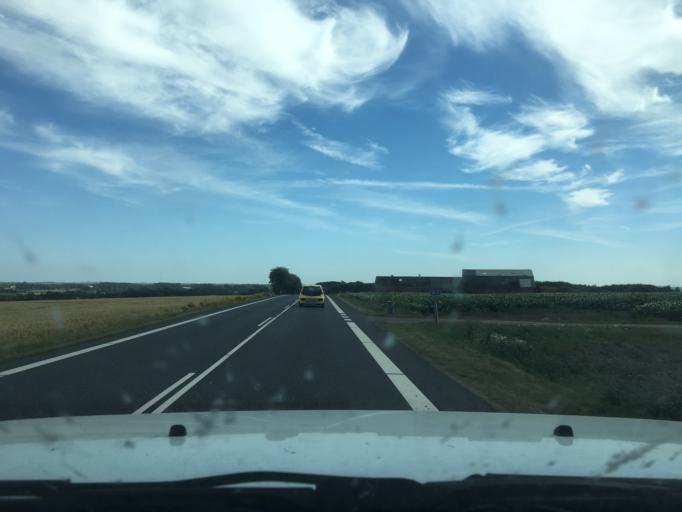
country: DK
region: Central Jutland
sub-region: Viborg Kommune
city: Viborg
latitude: 56.5881
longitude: 9.3681
